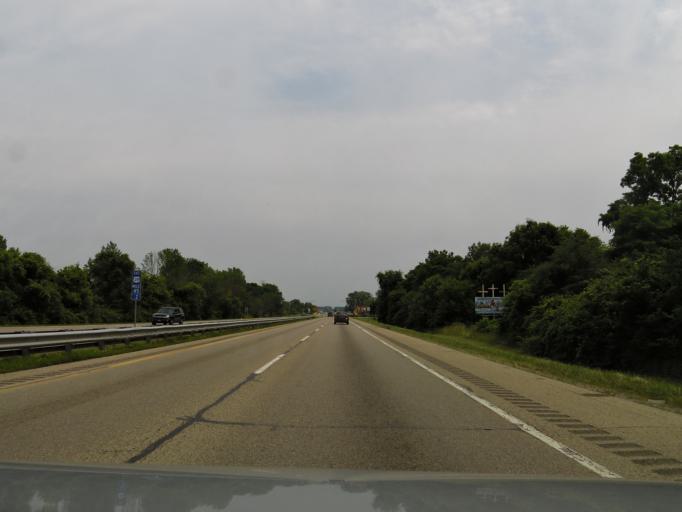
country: US
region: Ohio
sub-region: Greene County
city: Beavercreek
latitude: 39.7109
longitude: -84.0351
